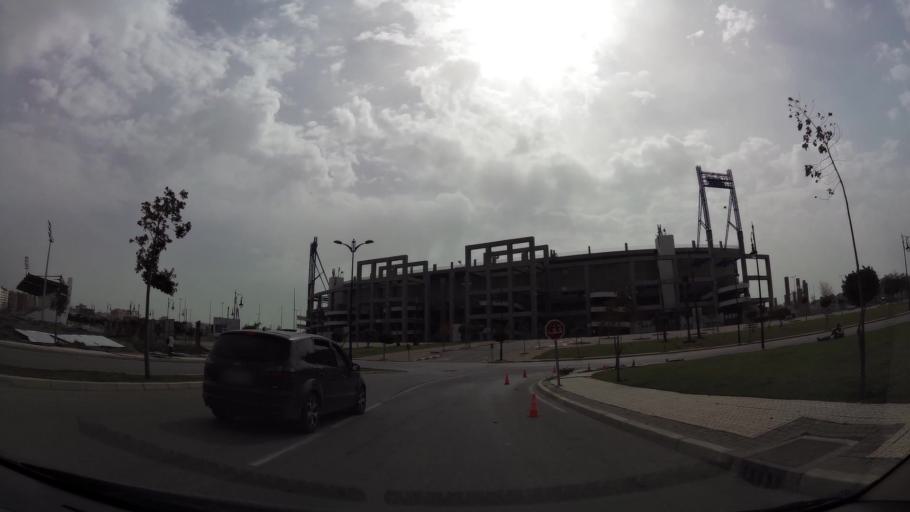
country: MA
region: Tanger-Tetouan
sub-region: Tanger-Assilah
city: Boukhalef
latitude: 35.7426
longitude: -5.8554
